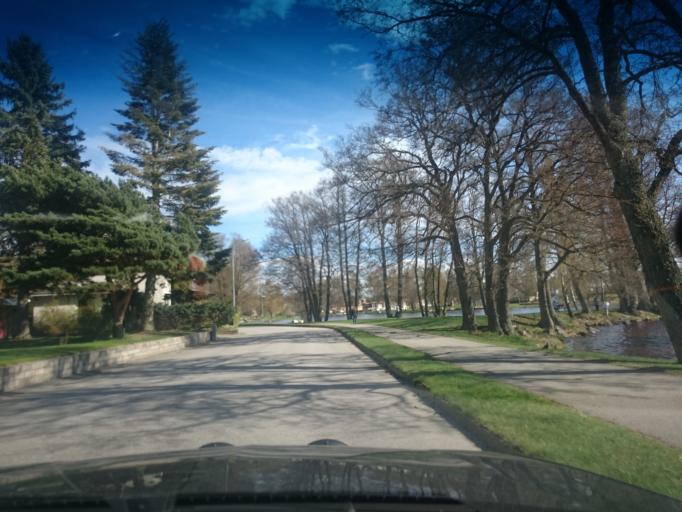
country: SE
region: Kalmar
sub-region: Hultsfreds Kommun
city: Virserum
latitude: 57.3198
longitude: 15.5766
